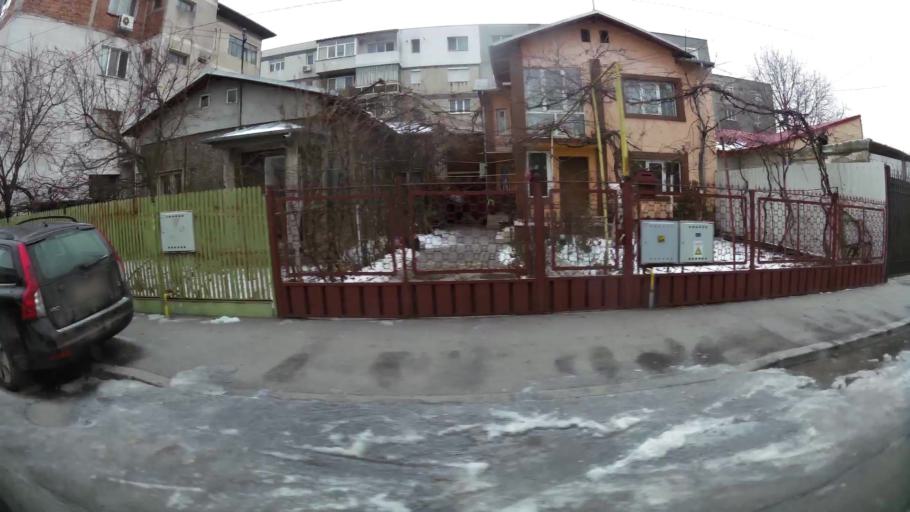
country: RO
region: Prahova
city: Ploiesti
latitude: 44.9433
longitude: 26.0375
